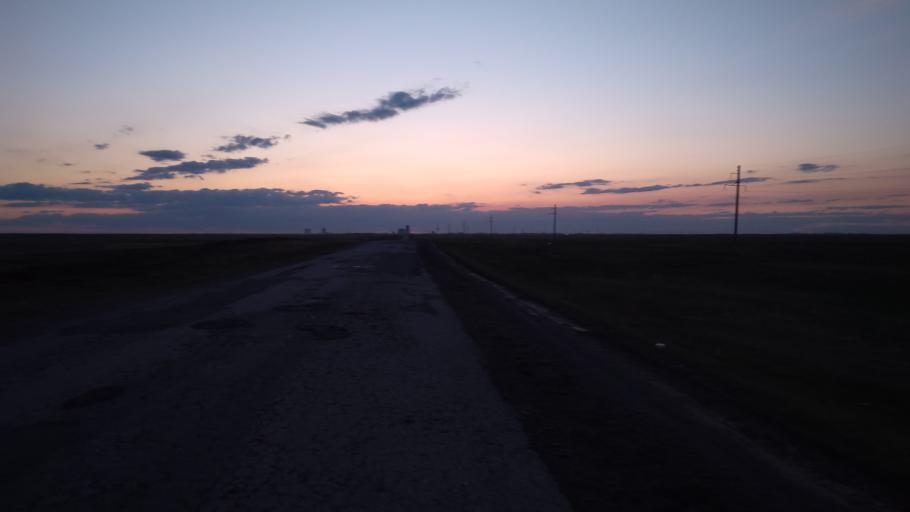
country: RU
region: Chelyabinsk
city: Troitsk
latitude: 54.0885
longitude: 61.6532
